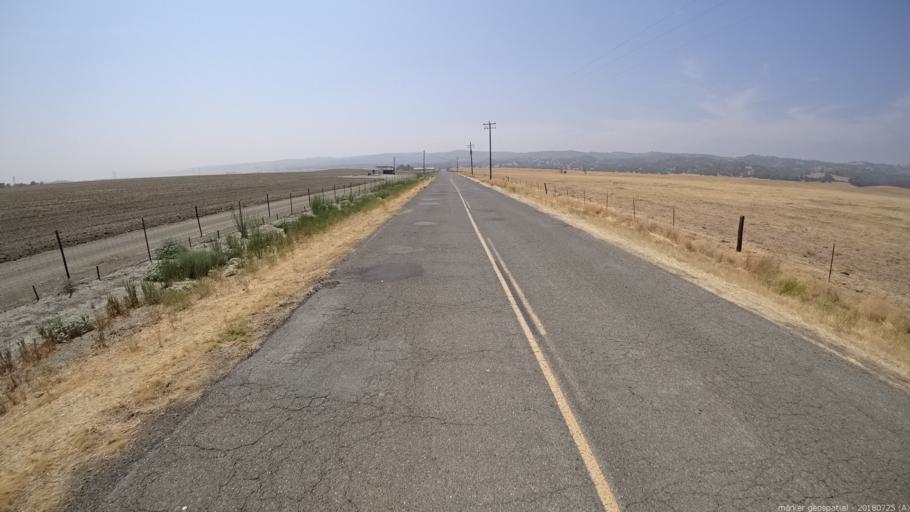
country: US
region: California
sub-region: San Luis Obispo County
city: Shandon
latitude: 35.8434
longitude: -120.3802
